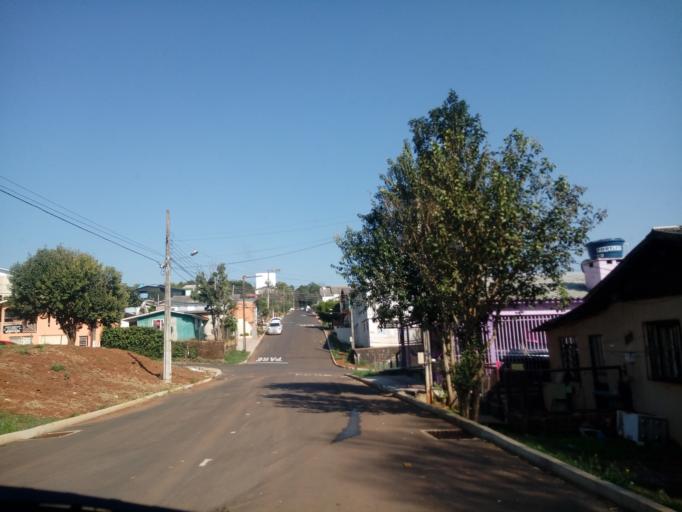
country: BR
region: Santa Catarina
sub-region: Chapeco
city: Chapeco
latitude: -27.0923
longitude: -52.6718
